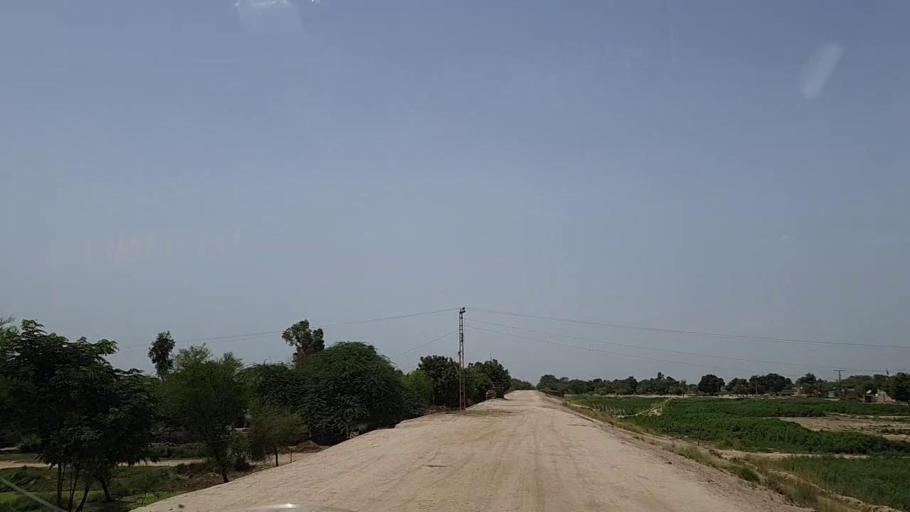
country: PK
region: Sindh
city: Tharu Shah
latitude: 27.0305
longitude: 68.1139
